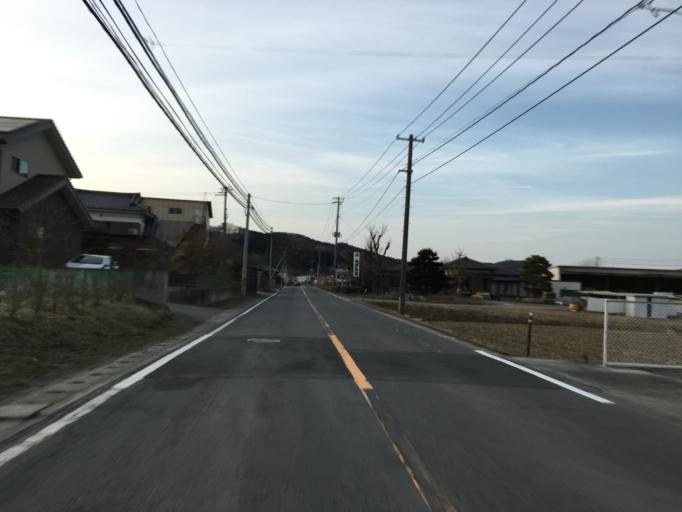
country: JP
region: Ibaraki
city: Daigo
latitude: 36.9349
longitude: 140.4077
